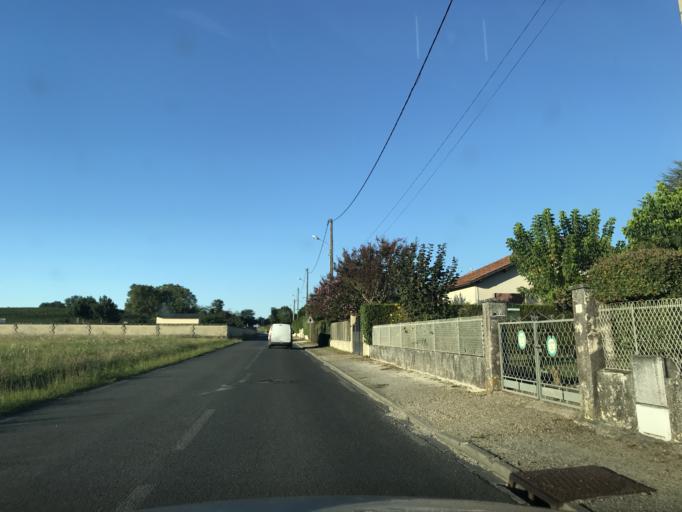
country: FR
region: Aquitaine
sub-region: Departement de la Gironde
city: Mouliets-et-Villemartin
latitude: 44.8619
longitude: -0.0557
